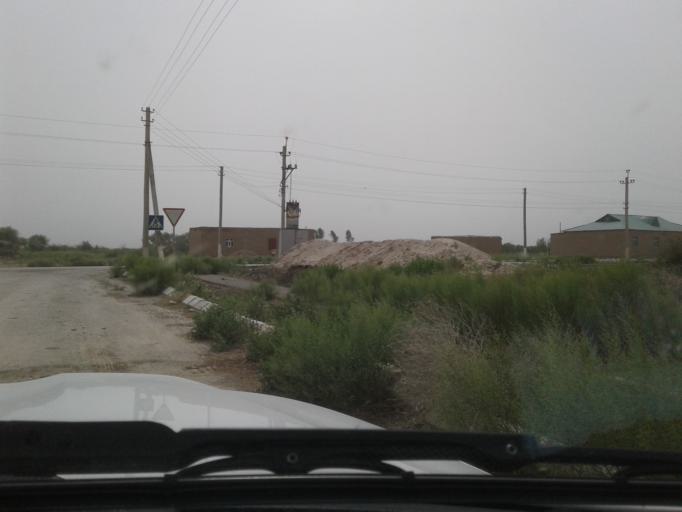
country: TM
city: Akdepe
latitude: 41.5942
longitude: 58.6128
